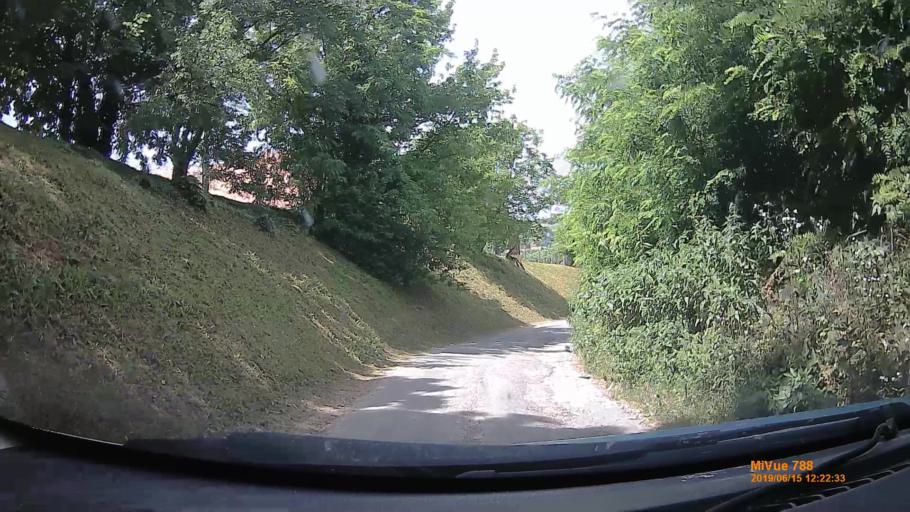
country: HU
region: Baranya
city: Buekkoesd
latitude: 46.1095
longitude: 18.0065
